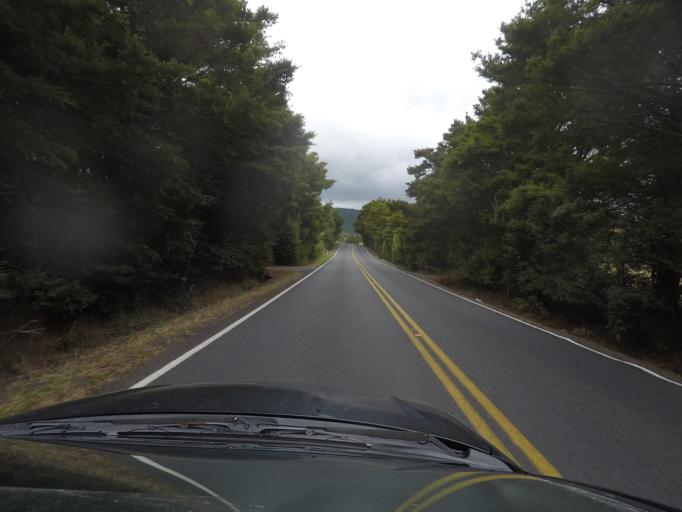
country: NZ
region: Auckland
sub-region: Auckland
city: Wellsford
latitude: -36.2874
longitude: 174.6302
